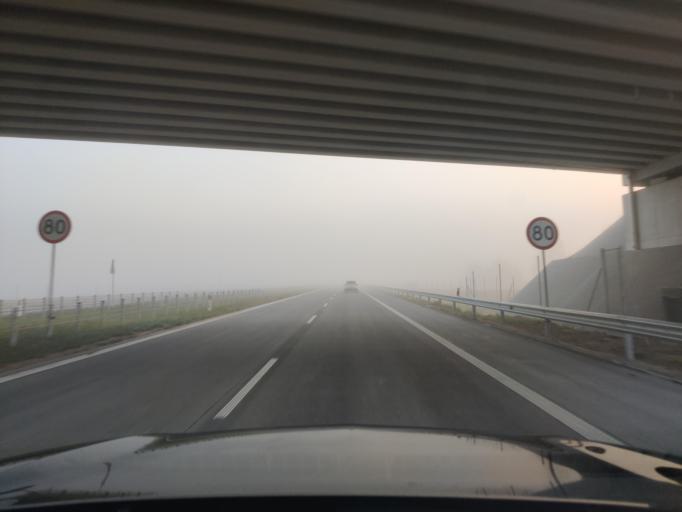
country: PL
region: Masovian Voivodeship
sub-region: Powiat mlawski
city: Strzegowo
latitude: 52.9623
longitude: 20.3114
